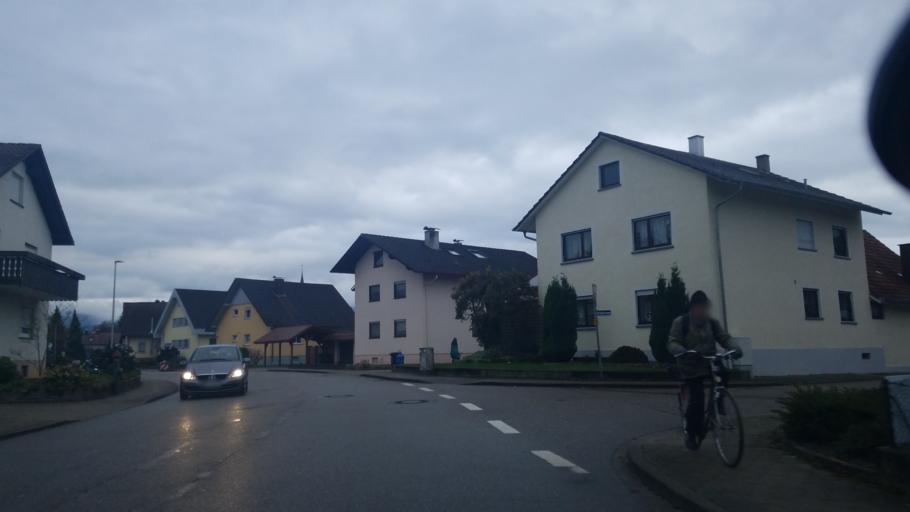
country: DE
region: Baden-Wuerttemberg
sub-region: Karlsruhe Region
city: Ottenhofen
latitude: 48.7215
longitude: 8.1137
